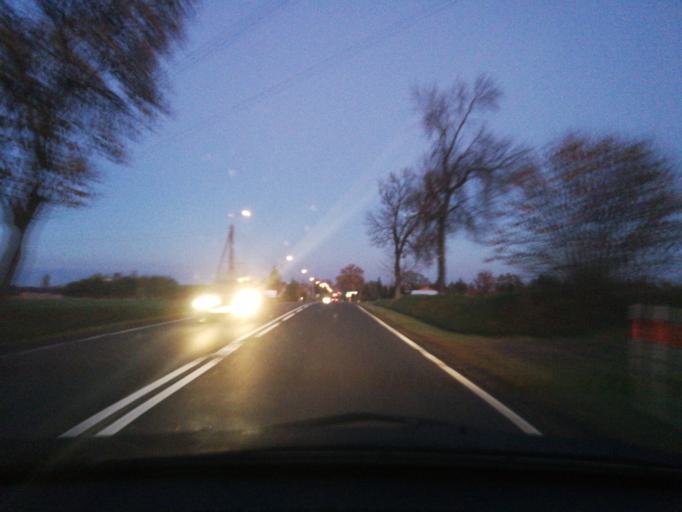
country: PL
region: Lodz Voivodeship
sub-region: Powiat brzezinski
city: Jezow
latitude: 51.8120
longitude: 19.9474
